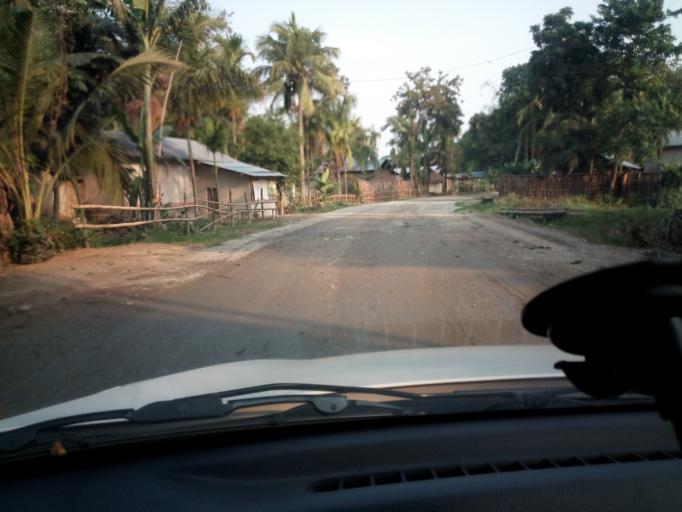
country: IN
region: Assam
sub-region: Udalguri
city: Udalguri
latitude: 26.7191
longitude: 92.0856
